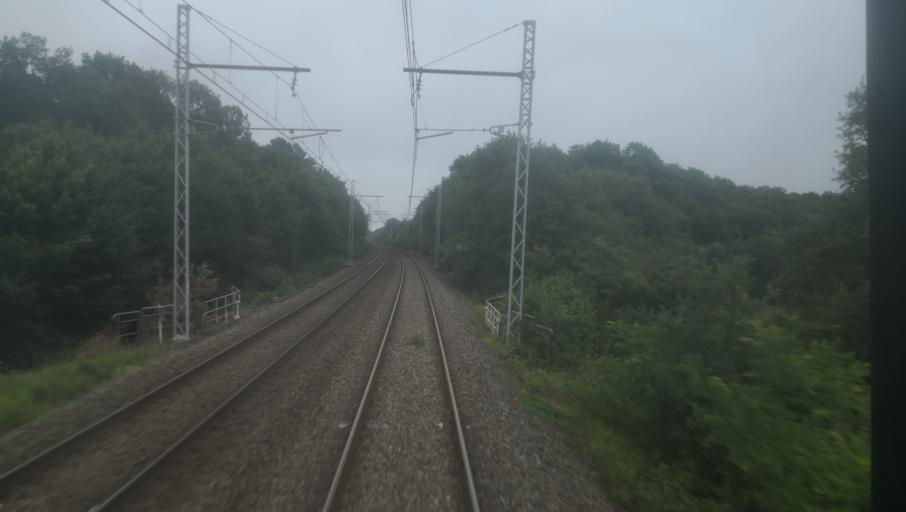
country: FR
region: Centre
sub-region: Departement de l'Indre
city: Luant
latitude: 46.6705
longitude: 1.5434
